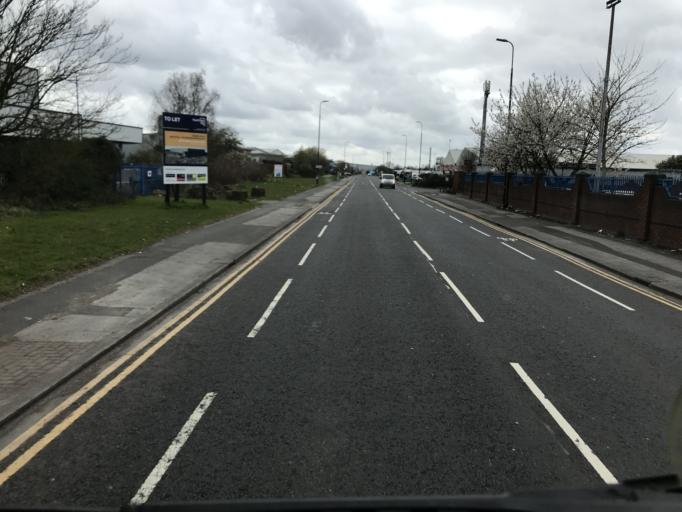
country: GB
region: England
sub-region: City and Borough of Salford
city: Eccles
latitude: 53.4706
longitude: -2.3279
